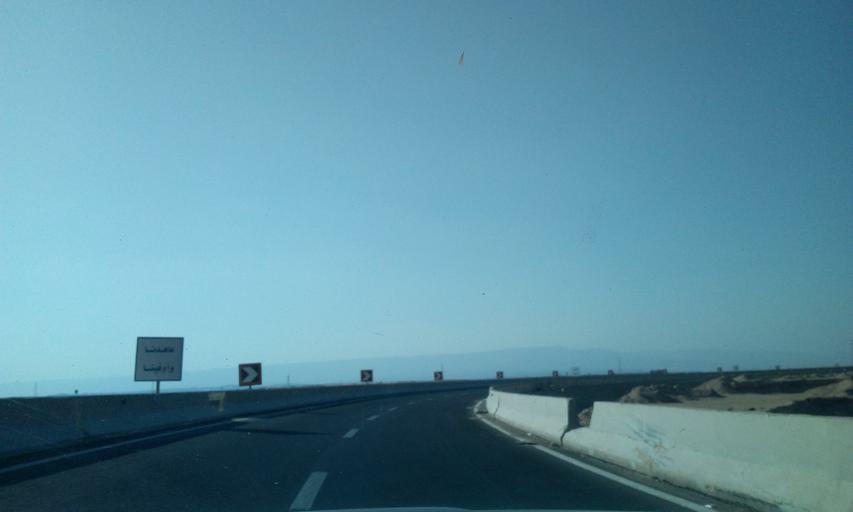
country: EG
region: As Suways
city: Ain Sukhna
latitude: 29.1058
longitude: 32.5307
